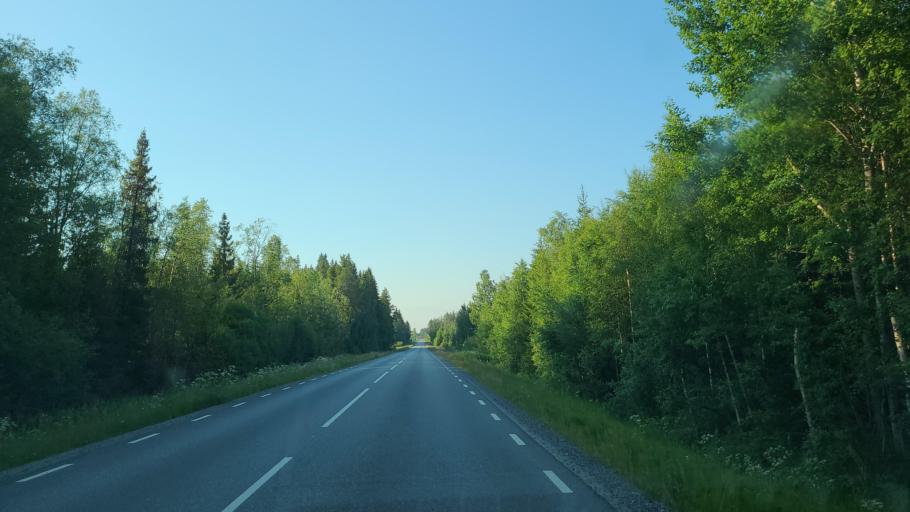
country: SE
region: Vaesterbotten
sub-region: Skelleftea Kommun
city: Burea
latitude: 64.4119
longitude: 21.3505
